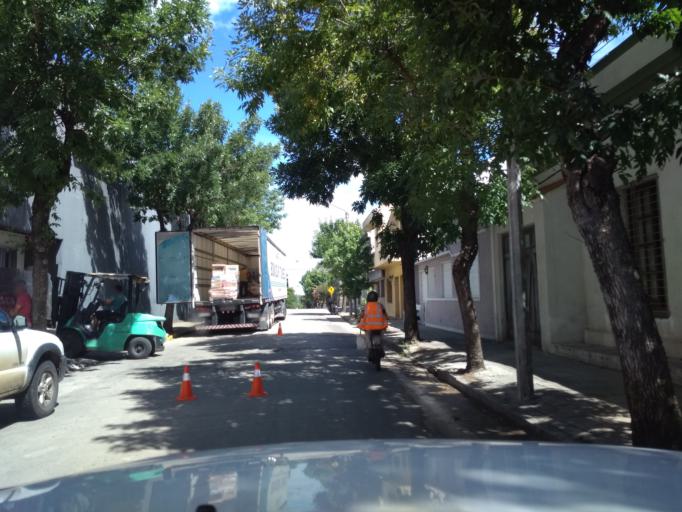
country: UY
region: Florida
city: Florida
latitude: -34.0960
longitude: -56.2153
